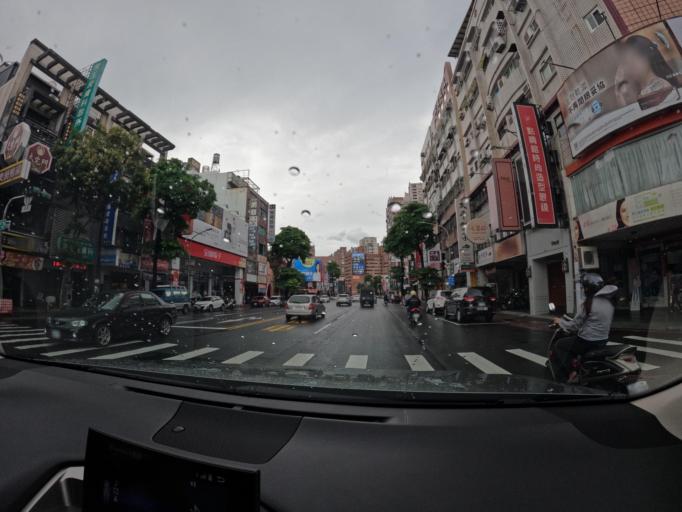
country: TW
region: Kaohsiung
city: Kaohsiung
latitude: 22.6660
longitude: 120.3088
